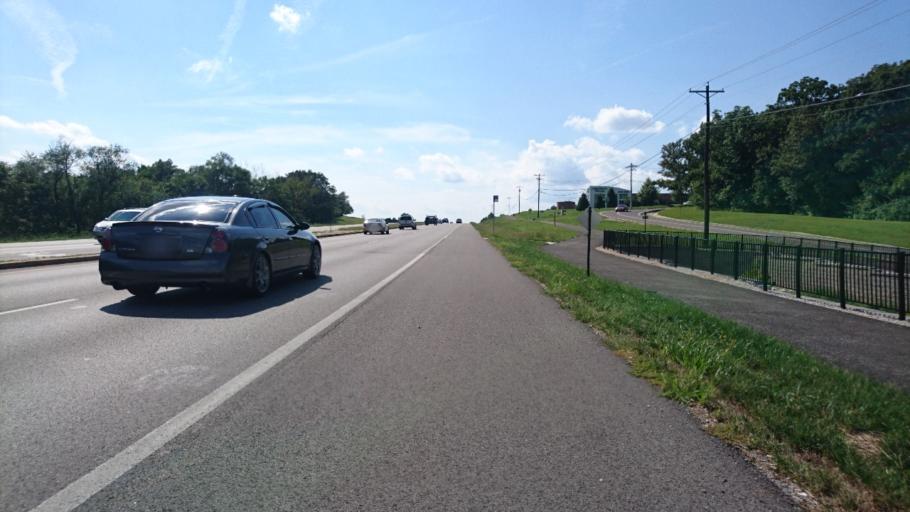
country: US
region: Missouri
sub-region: Saint Louis County
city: Ellisville
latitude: 38.5897
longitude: -90.5994
